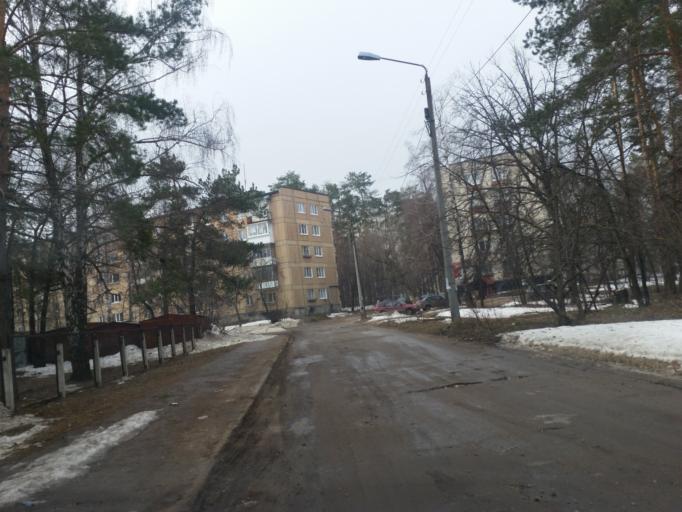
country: RU
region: Ulyanovsk
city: Dimitrovgrad
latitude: 54.2374
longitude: 49.5543
